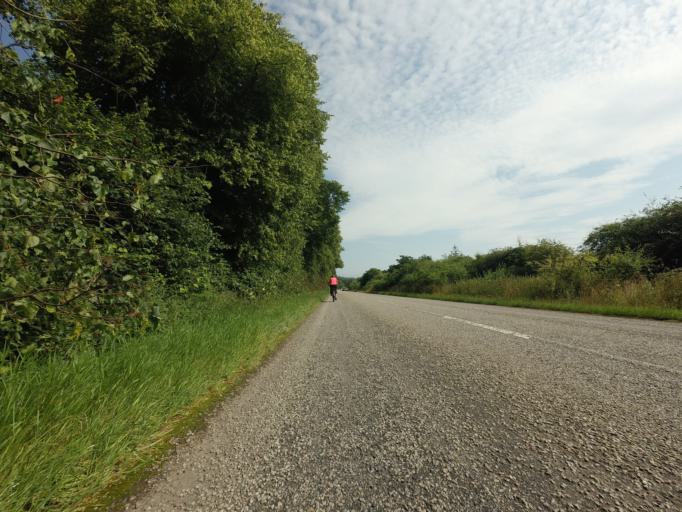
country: GB
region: Scotland
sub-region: Highland
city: Alness
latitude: 57.9127
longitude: -4.3783
